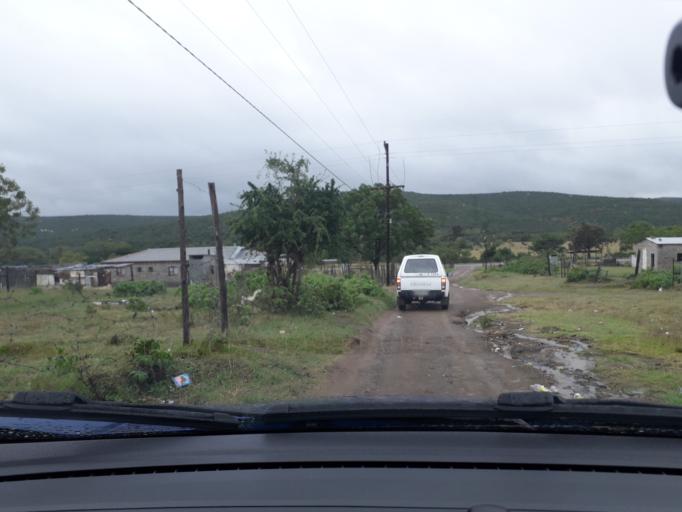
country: ZA
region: Eastern Cape
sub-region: Buffalo City Metropolitan Municipality
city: Bhisho
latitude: -32.8069
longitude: 27.3691
